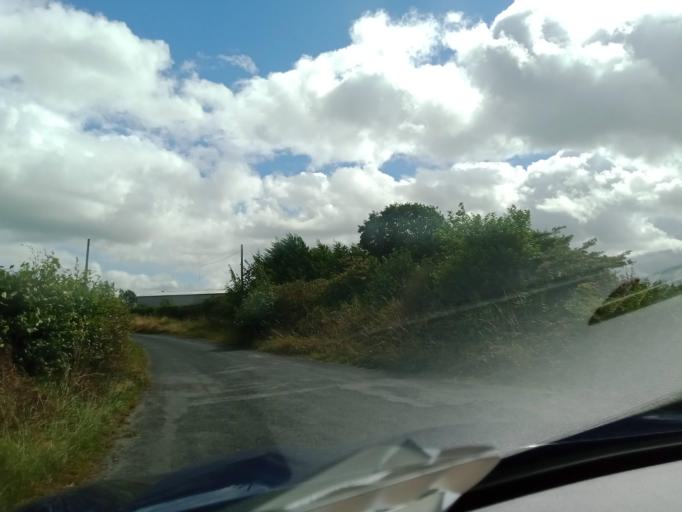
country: IE
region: Leinster
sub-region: Laois
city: Portlaoise
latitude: 53.0117
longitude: -7.2776
